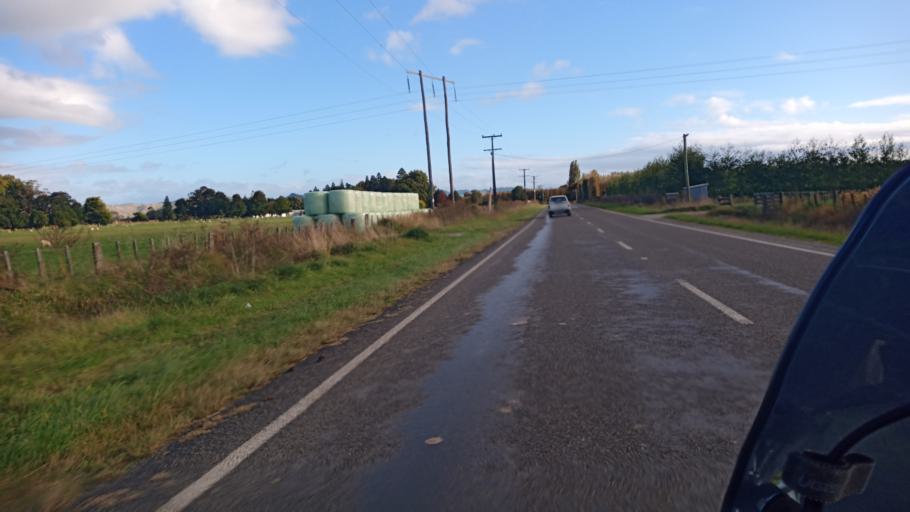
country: NZ
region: Gisborne
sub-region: Gisborne District
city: Gisborne
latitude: -38.6430
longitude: 177.9161
